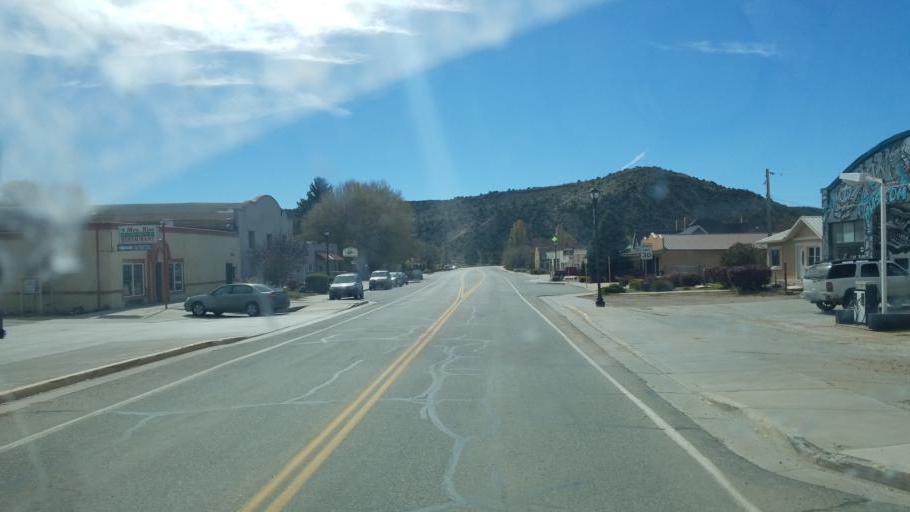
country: US
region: Colorado
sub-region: Costilla County
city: San Luis
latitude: 37.1977
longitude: -105.4271
